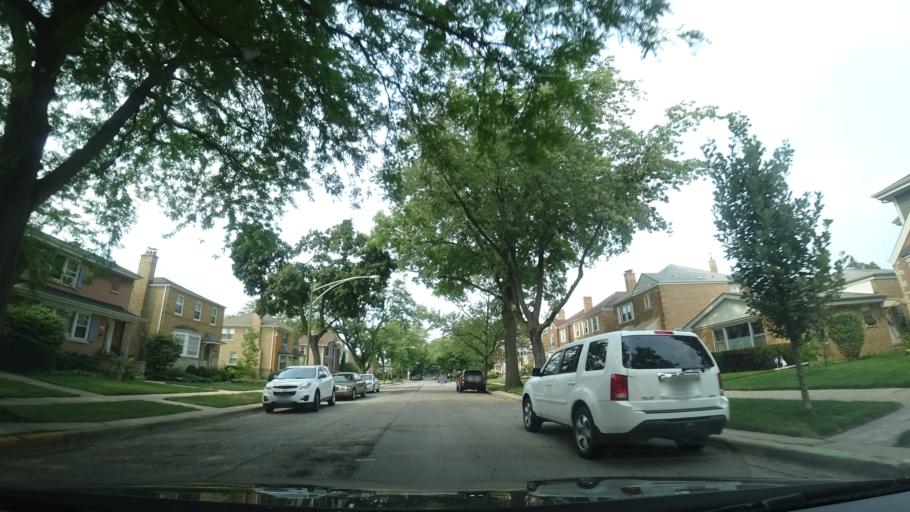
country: US
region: Illinois
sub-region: Cook County
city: Lincolnwood
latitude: 41.9926
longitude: -87.7350
